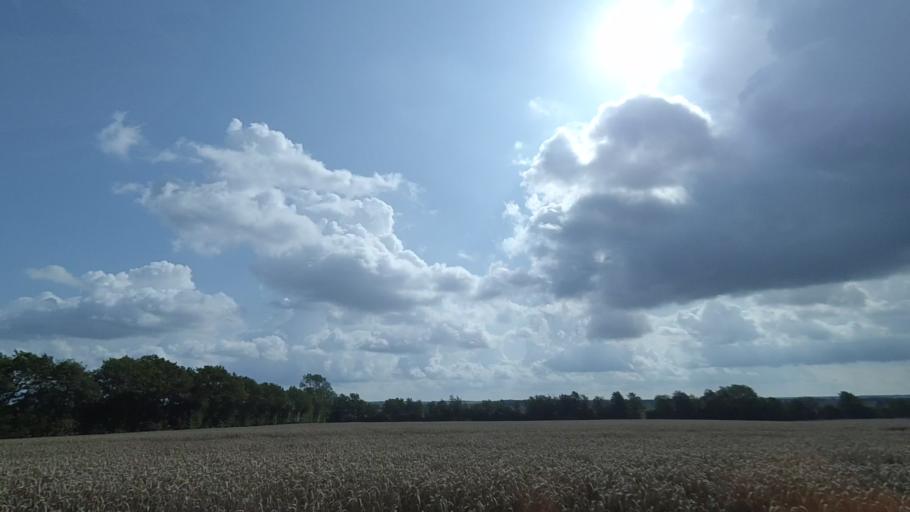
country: DK
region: Central Jutland
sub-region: Norddjurs Kommune
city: Allingabro
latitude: 56.5020
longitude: 10.3747
